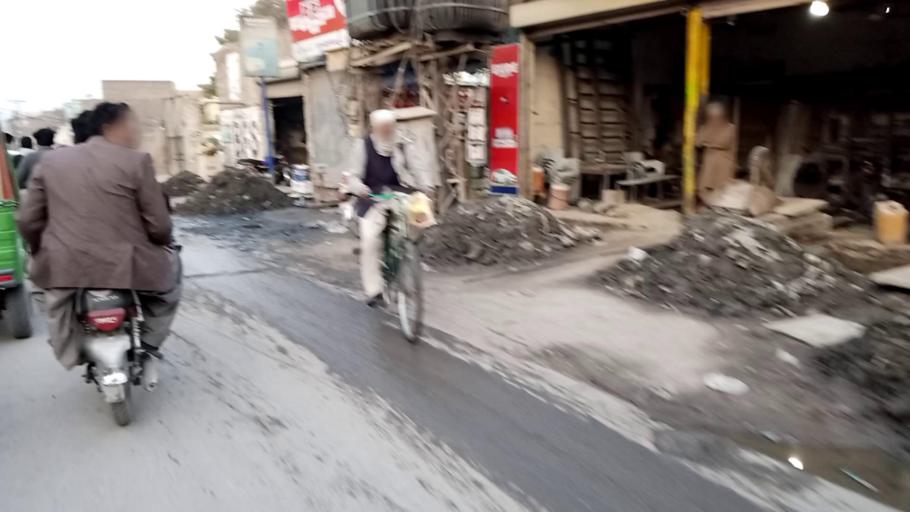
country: PK
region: Khyber Pakhtunkhwa
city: Peshawar
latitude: 34.0244
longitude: 71.4862
